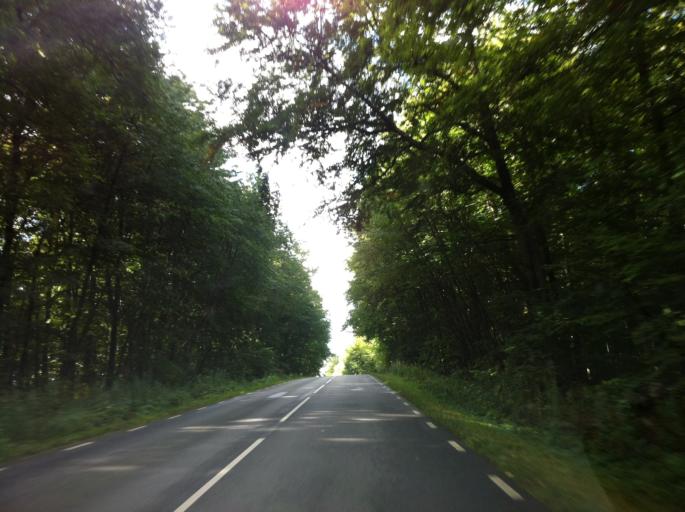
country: SE
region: Skane
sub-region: Tomelilla Kommun
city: Tomelilla
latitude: 55.6531
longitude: 13.9418
